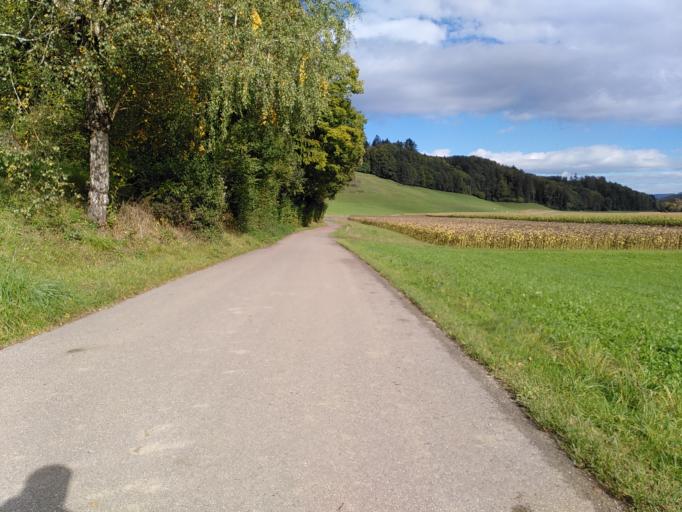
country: CH
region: Bern
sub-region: Oberaargau
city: Seeberg
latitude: 47.1497
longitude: 7.6912
